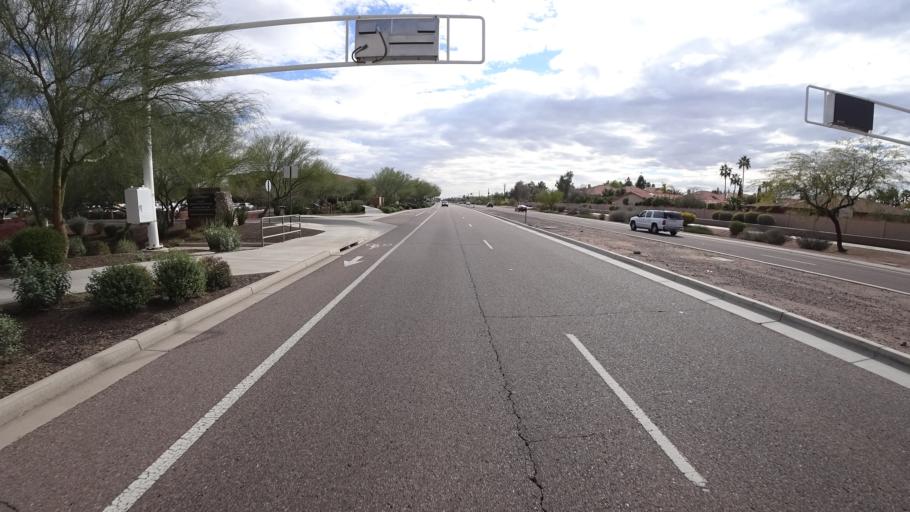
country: US
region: Arizona
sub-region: Maricopa County
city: Scottsdale
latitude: 33.5585
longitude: -111.8913
